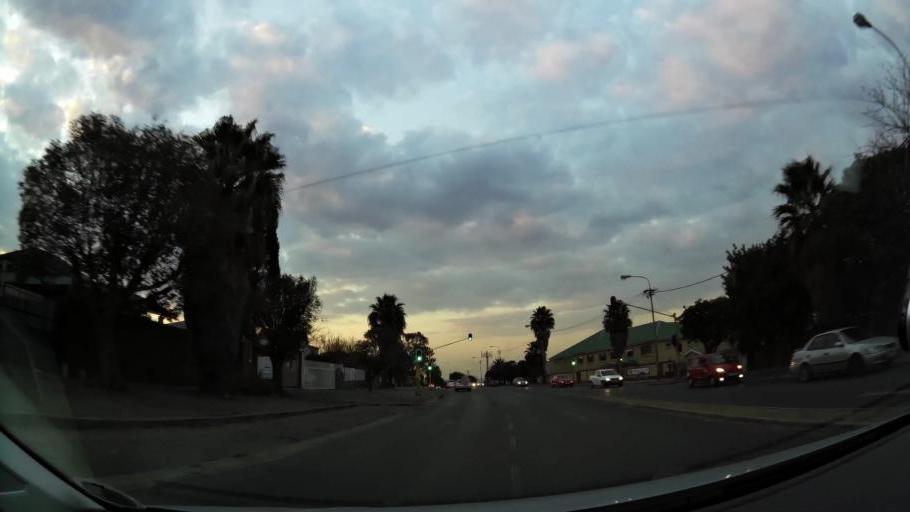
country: ZA
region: Gauteng
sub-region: Ekurhuleni Metropolitan Municipality
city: Germiston
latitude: -26.1971
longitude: 28.1296
